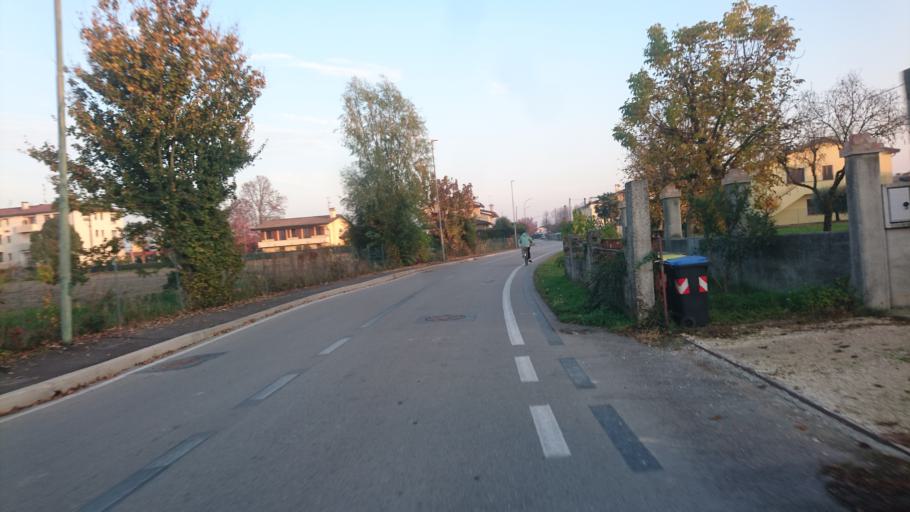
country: IT
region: Veneto
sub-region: Provincia di Padova
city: Terradura
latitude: 45.3498
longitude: 11.8164
